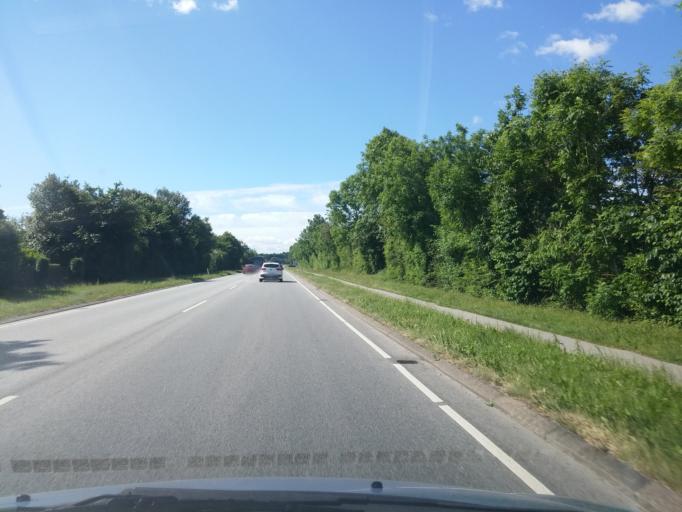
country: DK
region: South Denmark
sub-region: Haderslev Kommune
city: Haderslev
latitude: 55.2311
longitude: 9.4873
